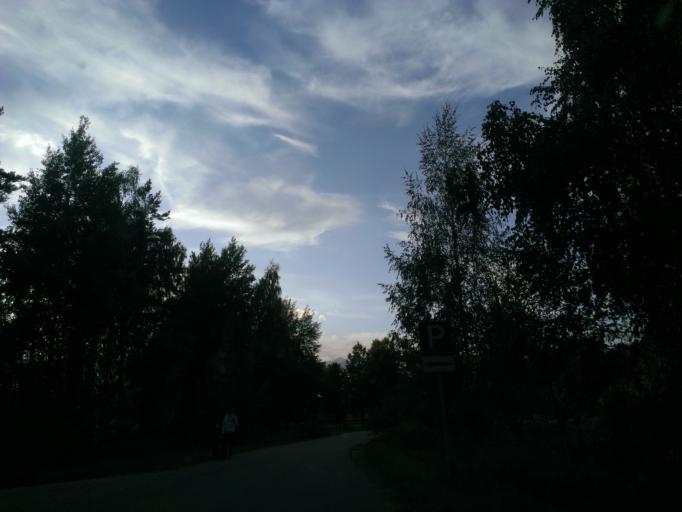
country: LV
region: Ikskile
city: Ikskile
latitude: 56.8402
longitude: 24.5062
